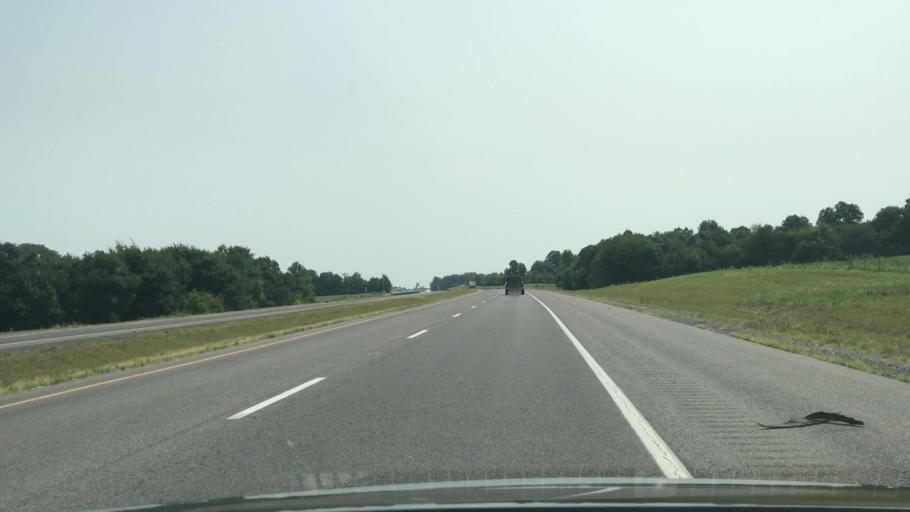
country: US
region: Kentucky
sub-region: Calloway County
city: Murray
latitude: 36.6490
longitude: -88.2430
